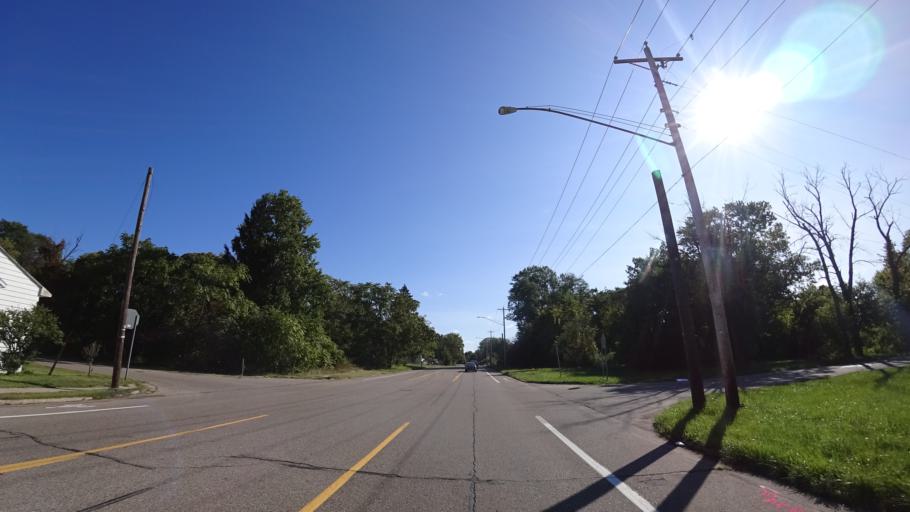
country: US
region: Michigan
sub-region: Berrien County
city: Benton Harbor
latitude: 42.1177
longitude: -86.4313
